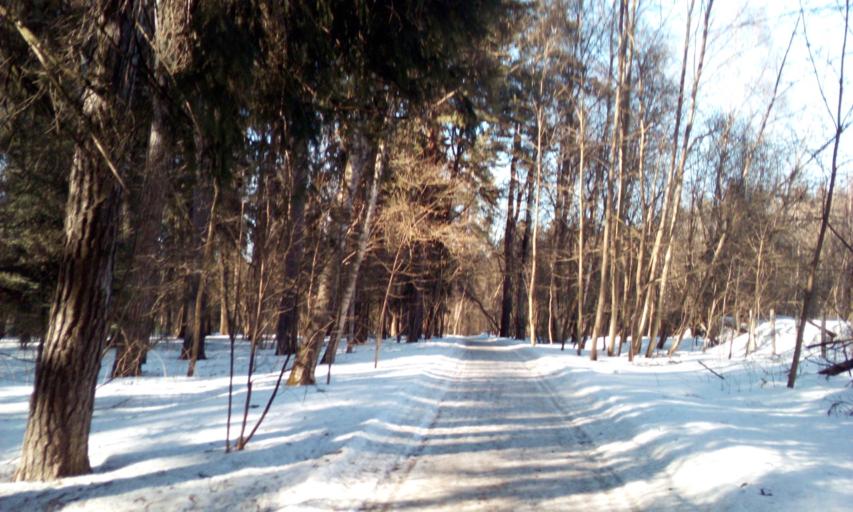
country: RU
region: Moscow
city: Novo-Peredelkino
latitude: 55.6642
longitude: 37.3480
